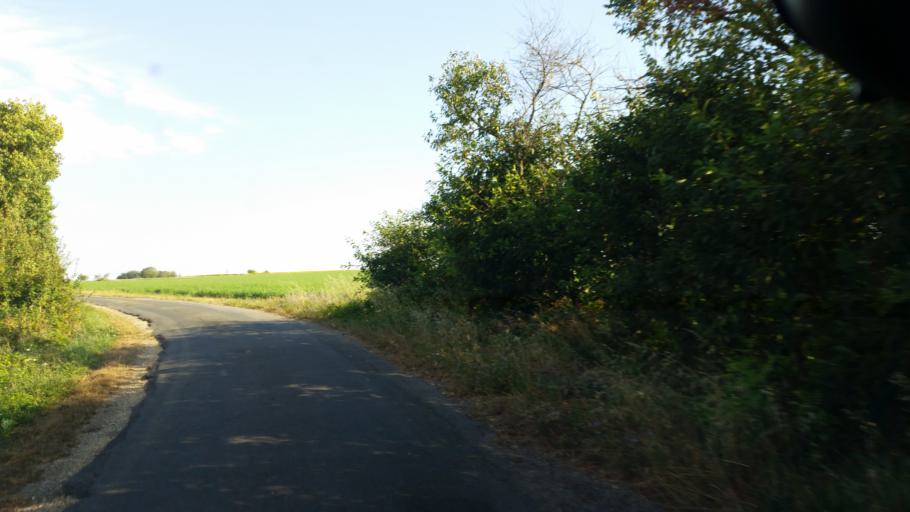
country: FR
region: Poitou-Charentes
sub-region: Departement de la Charente-Maritime
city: Saint-Jean-de-Liversay
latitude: 46.2311
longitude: -0.8888
